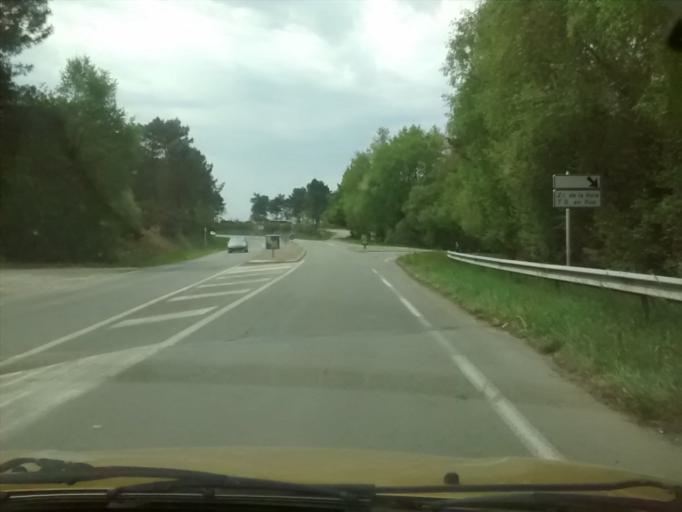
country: FR
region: Brittany
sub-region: Departement du Morbihan
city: Berric
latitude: 47.6028
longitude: -2.5472
